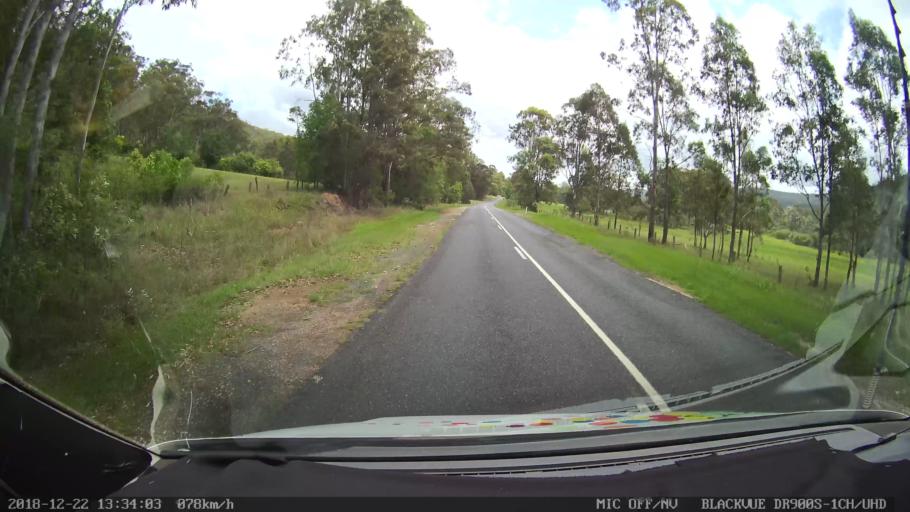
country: AU
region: New South Wales
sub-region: Clarence Valley
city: Coutts Crossing
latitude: -29.8674
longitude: 152.8216
